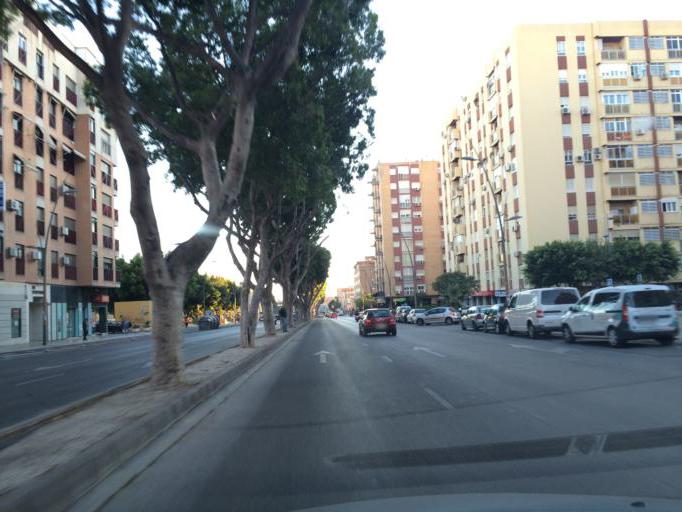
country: ES
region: Andalusia
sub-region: Provincia de Almeria
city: Almeria
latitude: 36.8429
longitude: -2.4473
